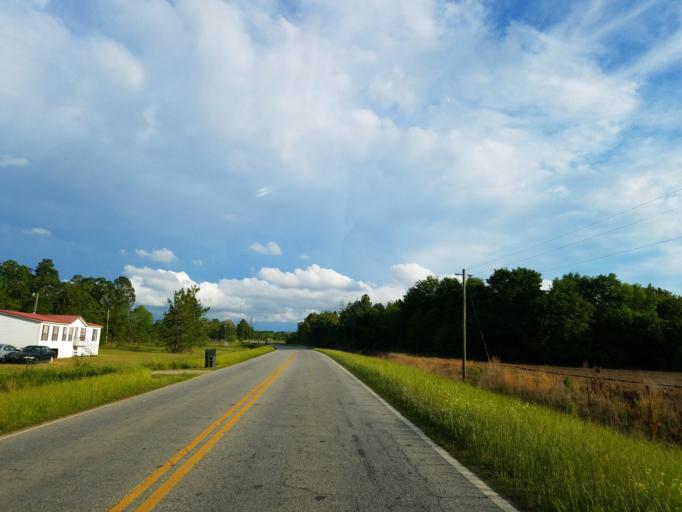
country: US
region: Georgia
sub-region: Crisp County
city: Cordele
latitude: 31.9406
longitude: -83.7869
